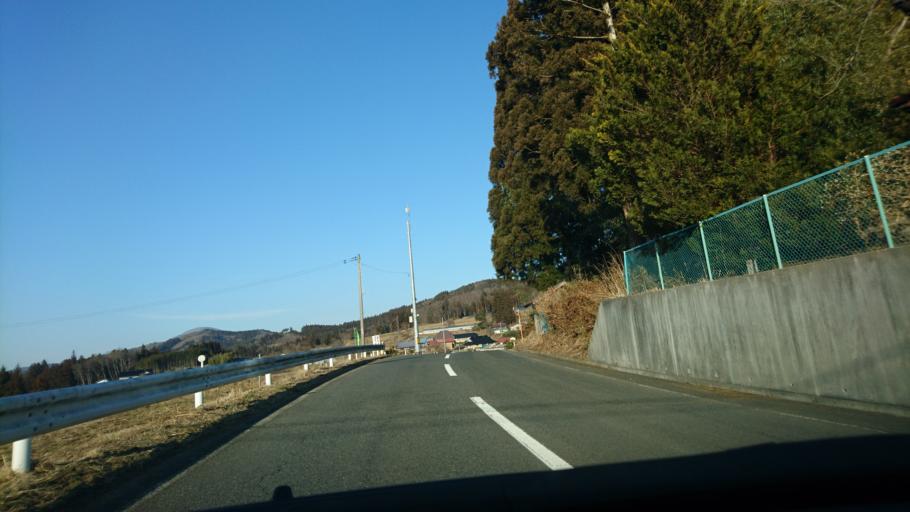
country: JP
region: Iwate
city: Ichinoseki
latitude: 38.8884
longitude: 141.3966
